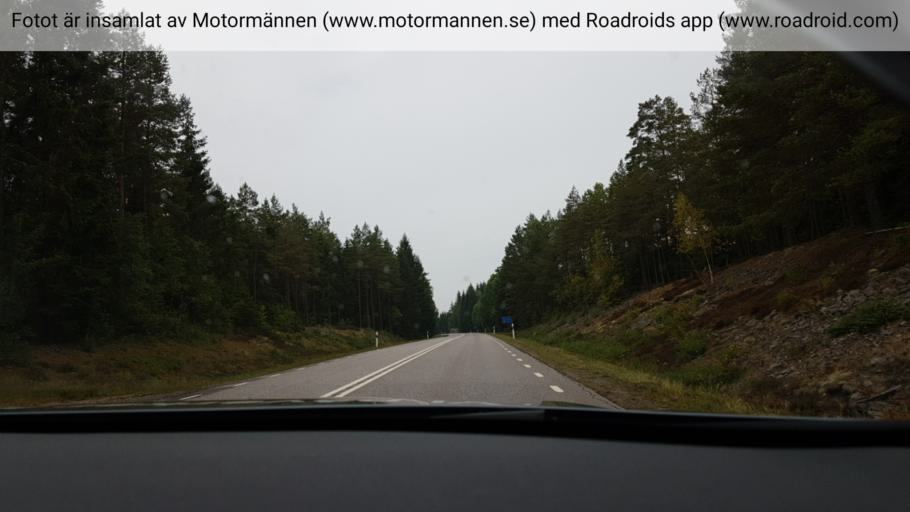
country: SE
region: Joenkoeping
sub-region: Varnamo Kommun
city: Bor
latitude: 57.2420
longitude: 14.1666
